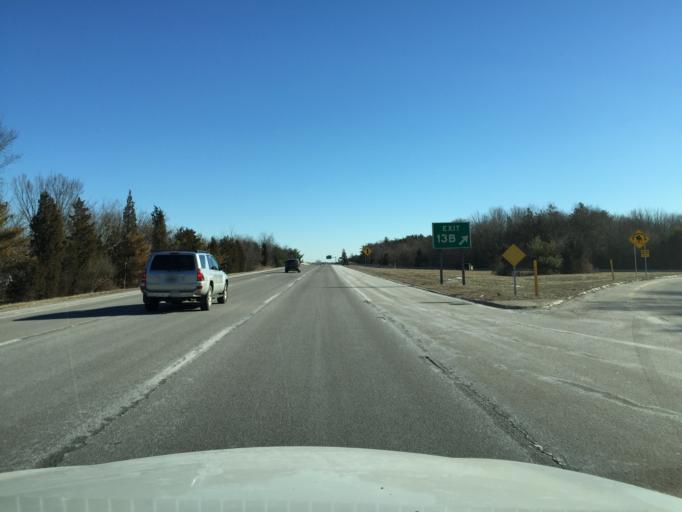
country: US
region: Massachusetts
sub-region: Norfolk County
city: Foxborough
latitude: 42.0283
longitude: -71.2613
